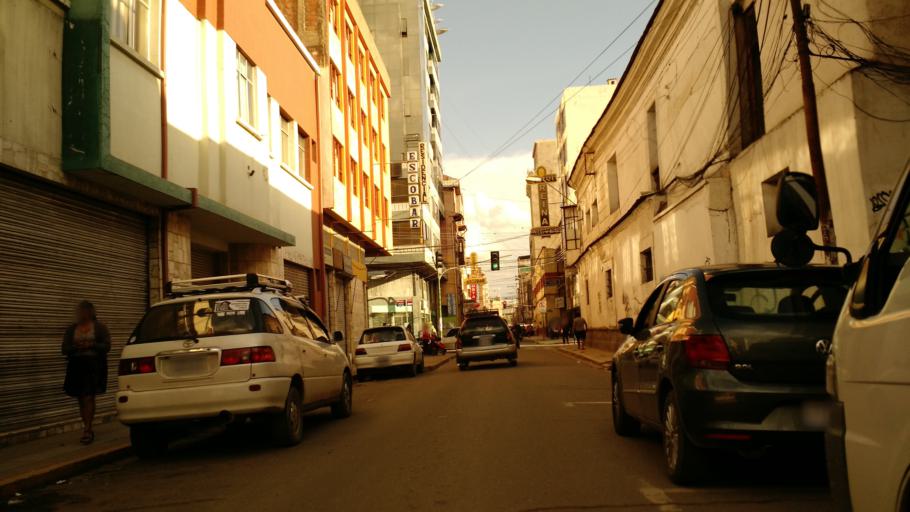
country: BO
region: Cochabamba
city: Cochabamba
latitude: -17.3981
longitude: -66.1567
